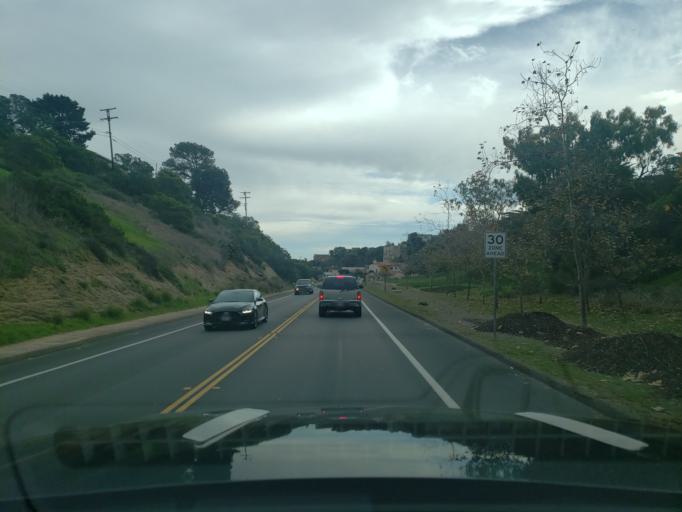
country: US
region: California
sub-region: San Diego County
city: Coronado
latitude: 32.7261
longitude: -117.2376
